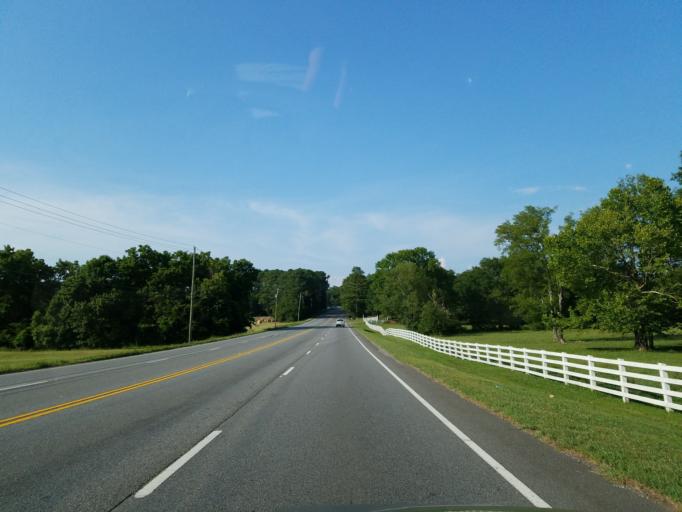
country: US
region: Georgia
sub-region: Bartow County
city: Cartersville
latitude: 34.2278
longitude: -84.7858
